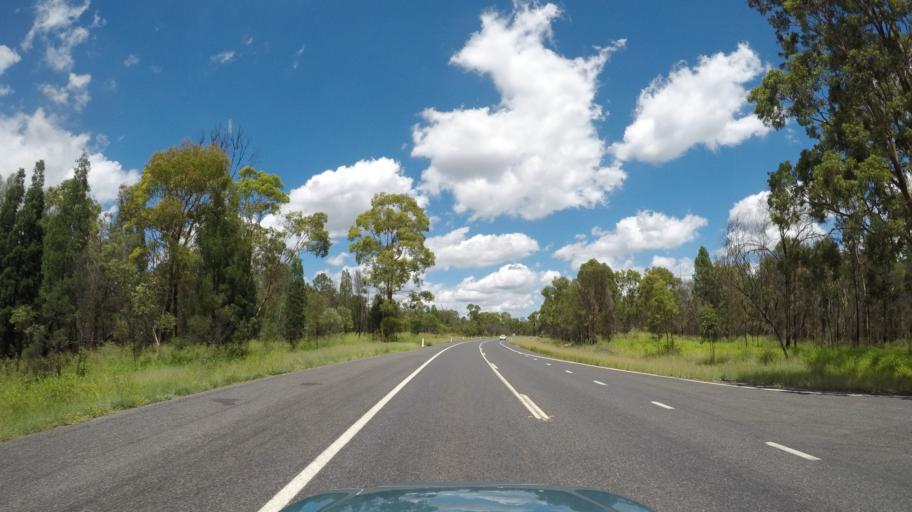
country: AU
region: Queensland
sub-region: Western Downs
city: Dalby
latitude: -27.9769
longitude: 151.0918
